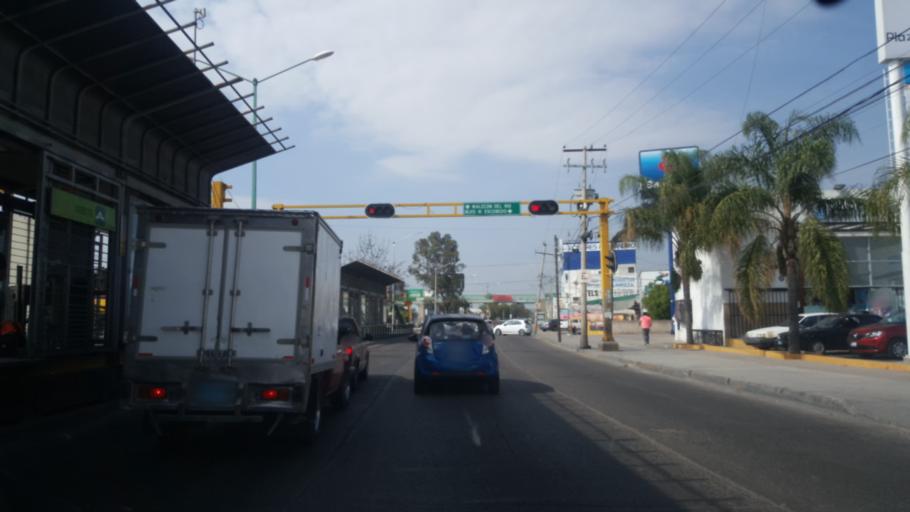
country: MX
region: Guanajuato
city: Leon
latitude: 21.0968
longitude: -101.6489
